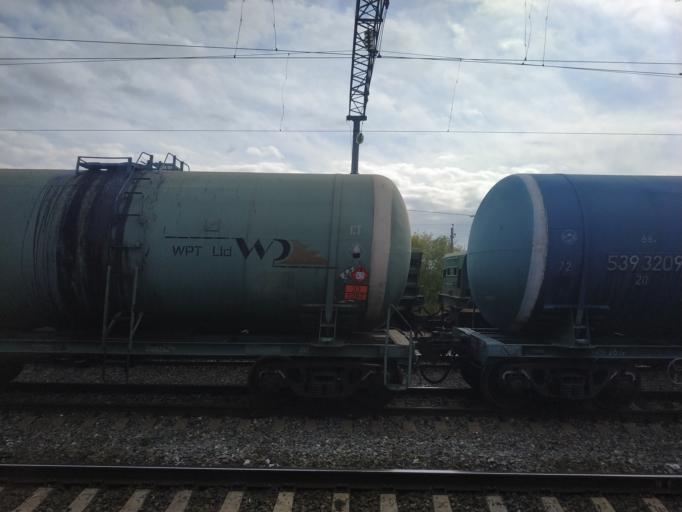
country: RU
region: Volgograd
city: Volgograd
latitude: 48.6699
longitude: 44.4614
